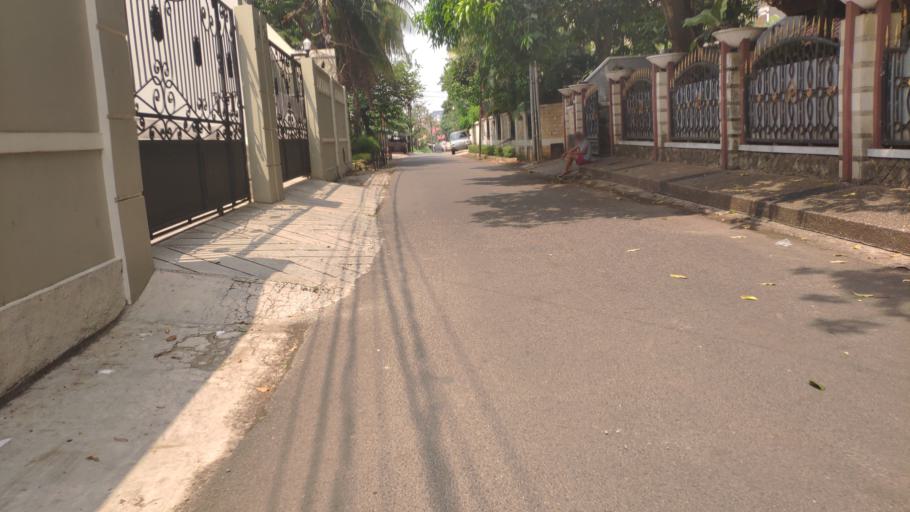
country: ID
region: Jakarta Raya
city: Jakarta
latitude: -6.2709
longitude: 106.8257
